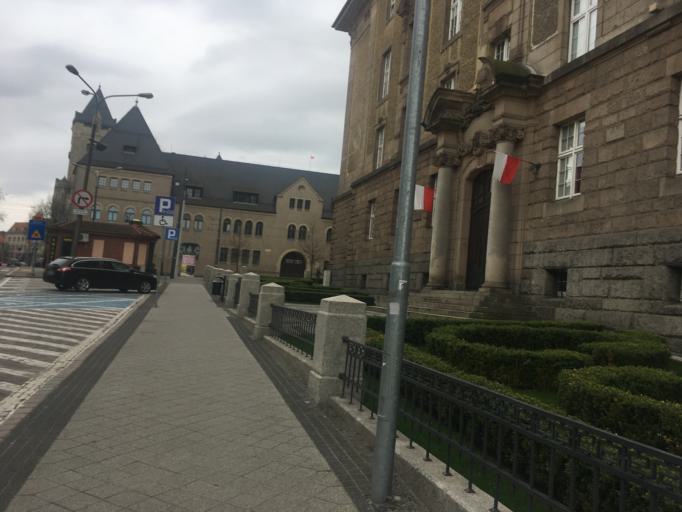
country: PL
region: Greater Poland Voivodeship
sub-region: Poznan
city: Poznan
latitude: 52.4097
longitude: 16.9199
